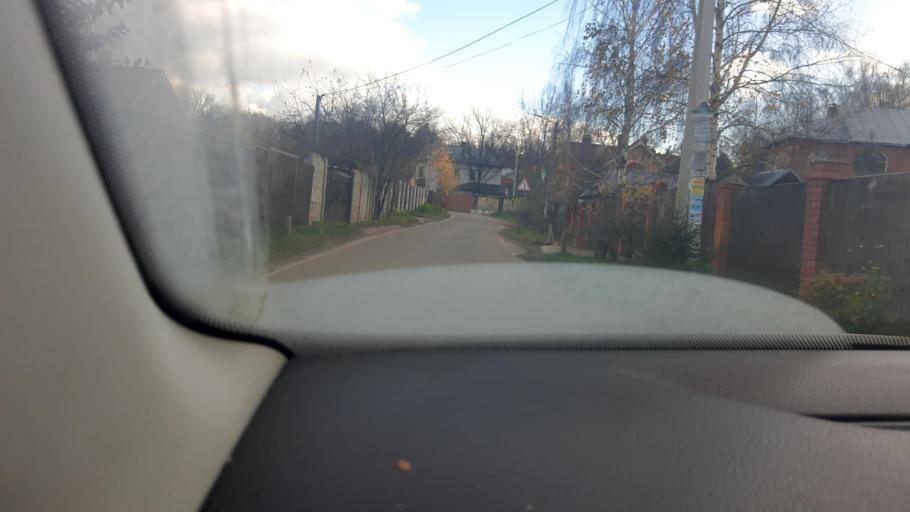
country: RU
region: Moskovskaya
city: Biryulevo Zapadnoye
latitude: 55.5545
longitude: 37.6259
